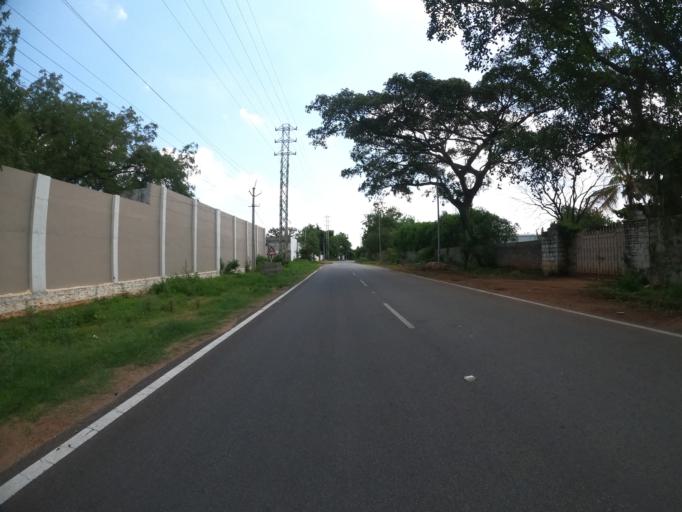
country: IN
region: Telangana
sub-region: Rangareddi
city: Sriramnagar
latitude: 17.3646
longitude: 78.3240
